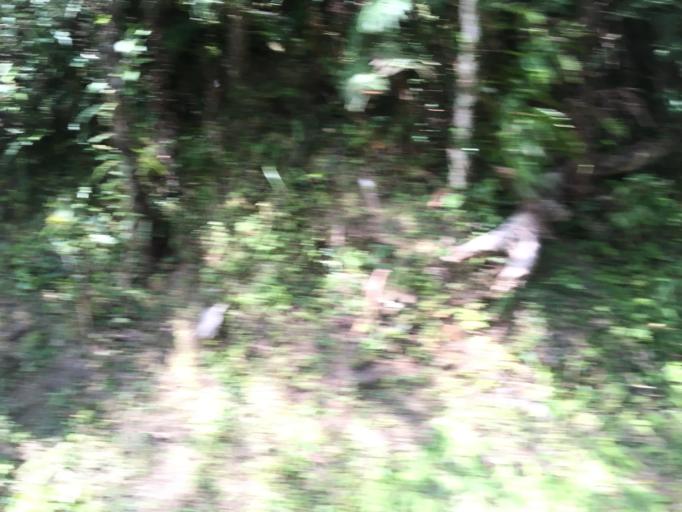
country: TW
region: Taiwan
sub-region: Yilan
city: Yilan
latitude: 24.7570
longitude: 121.6139
